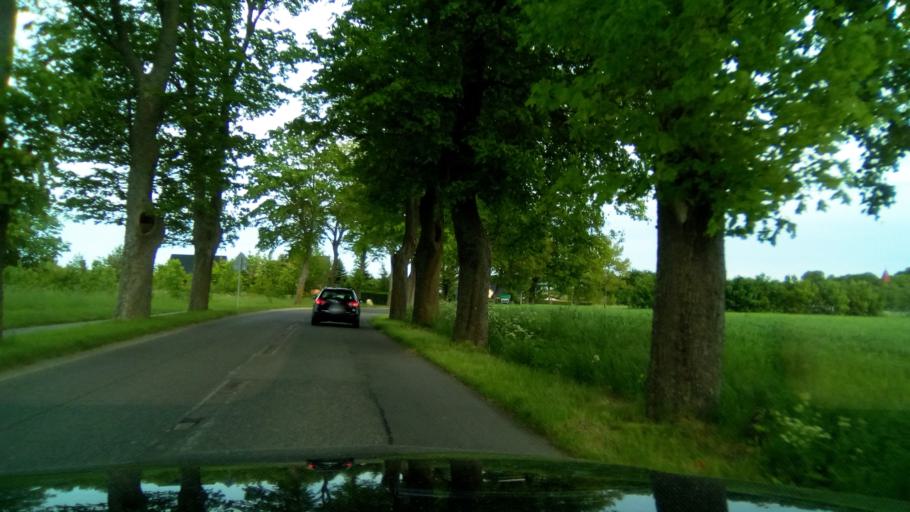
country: PL
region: Pomeranian Voivodeship
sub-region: Powiat pucki
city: Wierzchucino
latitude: 54.7906
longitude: 17.9881
